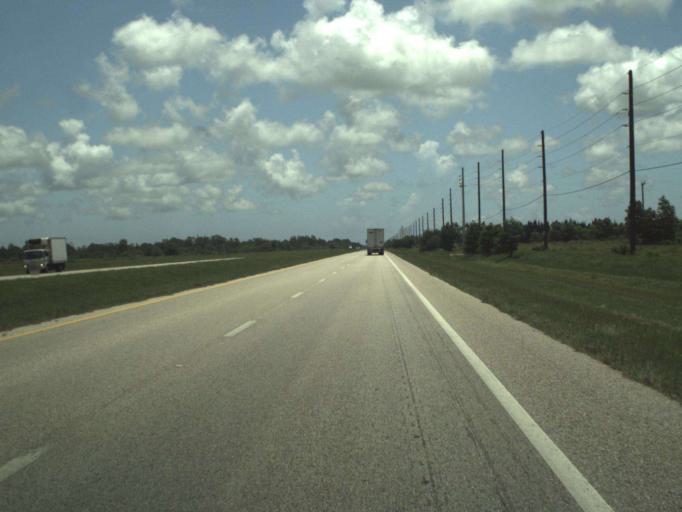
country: US
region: Florida
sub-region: Indian River County
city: West Vero Corridor
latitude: 27.6397
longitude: -80.5862
